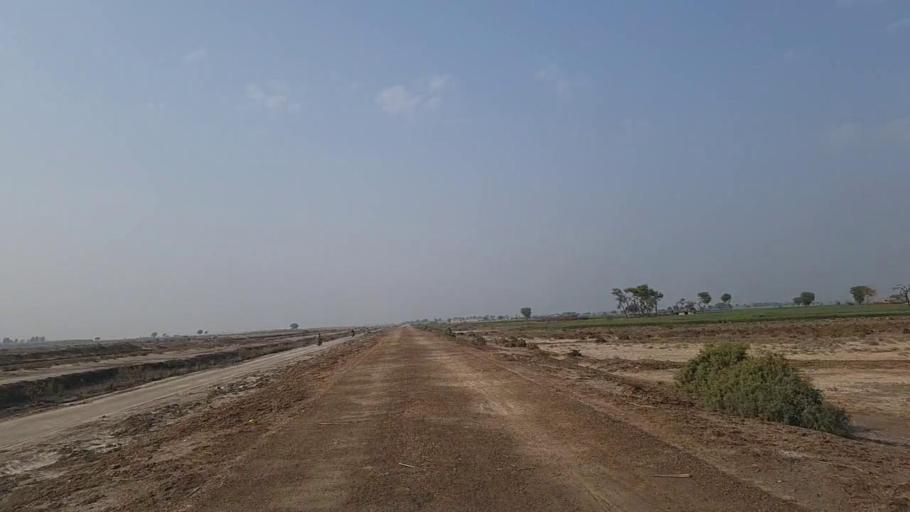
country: PK
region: Sindh
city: Nawabshah
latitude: 26.3283
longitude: 68.4779
